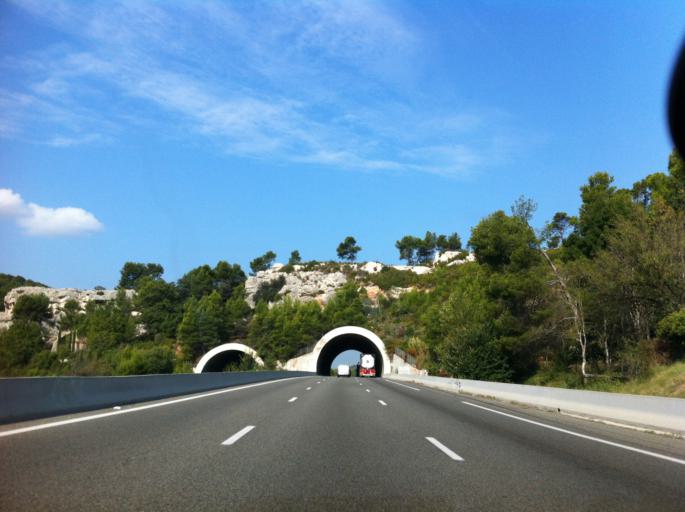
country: FR
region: Provence-Alpes-Cote d'Azur
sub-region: Departement des Bouches-du-Rhone
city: Le Tholonet
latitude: 43.5049
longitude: 5.5114
